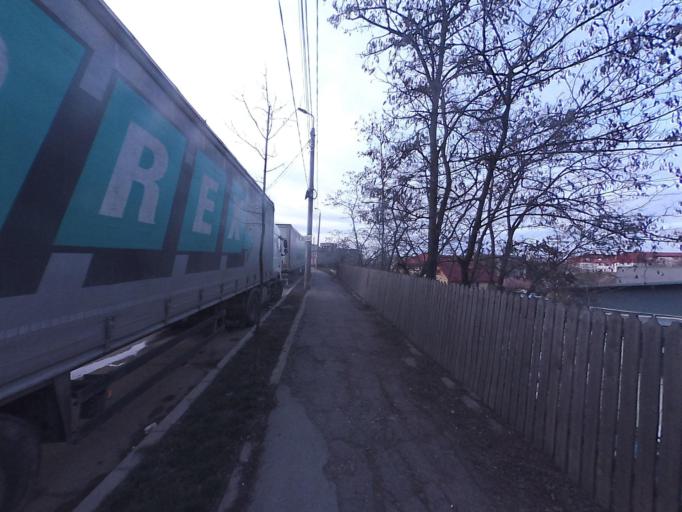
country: RO
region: Iasi
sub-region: Municipiul Iasi
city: Iasi
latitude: 47.1354
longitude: 27.5835
